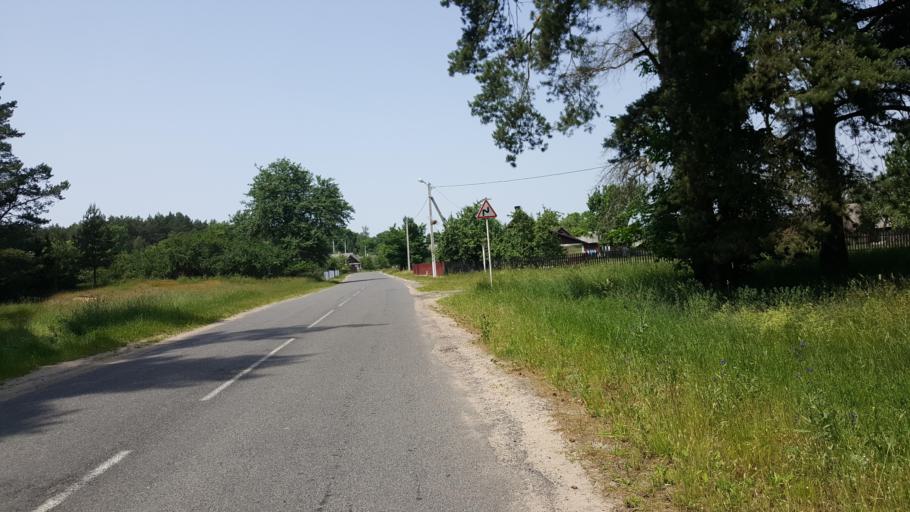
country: BY
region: Brest
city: Kamyanyuki
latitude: 52.5044
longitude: 23.8608
